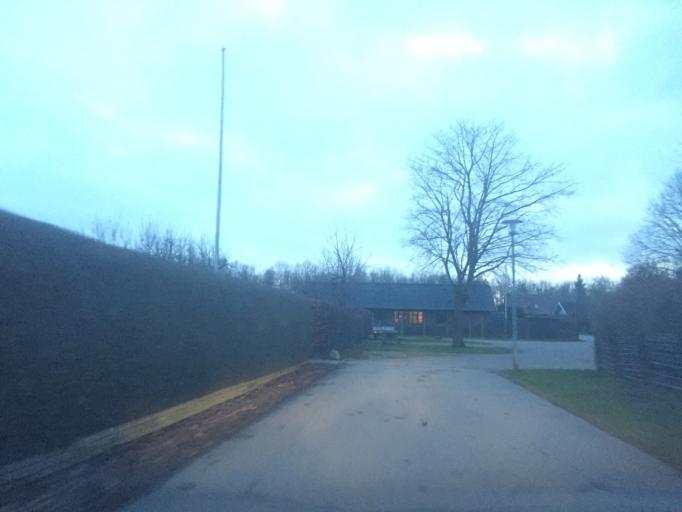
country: DK
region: Capital Region
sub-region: Hoje-Taastrup Kommune
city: Flong
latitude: 55.6431
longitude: 12.1982
